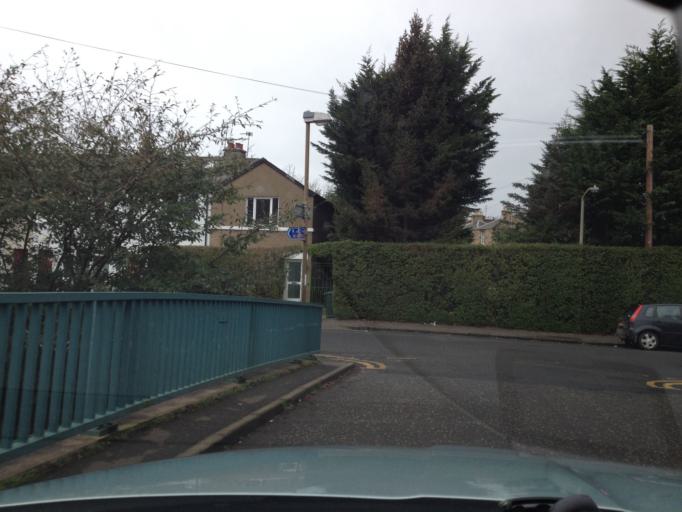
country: GB
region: Scotland
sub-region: Edinburgh
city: Colinton
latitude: 55.9445
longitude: -3.2438
